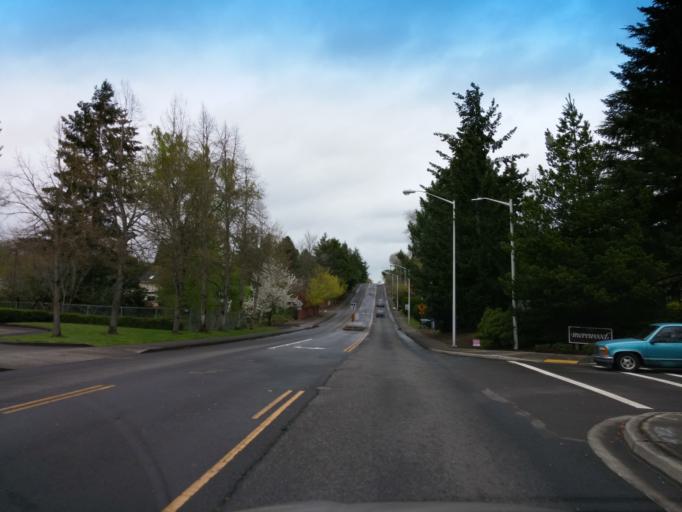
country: US
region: Oregon
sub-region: Washington County
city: Oak Hills
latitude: 45.5264
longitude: -122.8547
